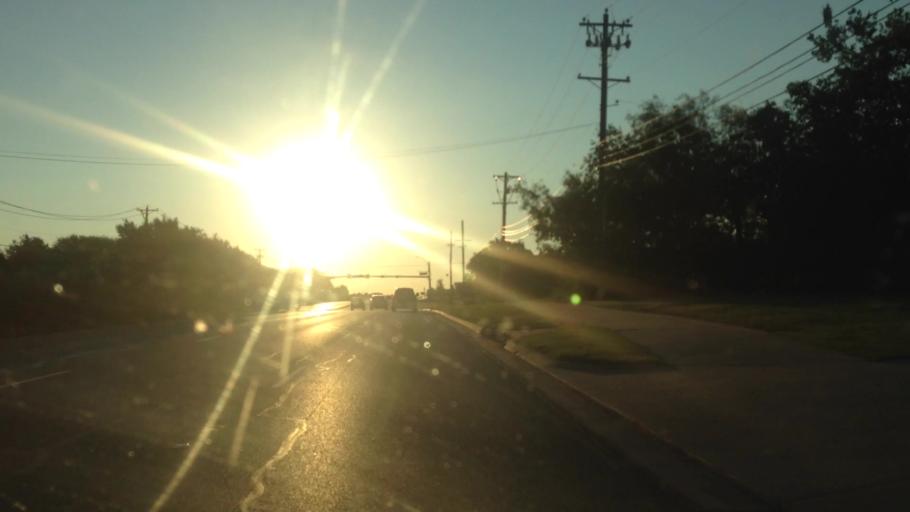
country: US
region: Texas
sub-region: Tarrant County
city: Southlake
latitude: 32.9410
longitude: -97.1391
